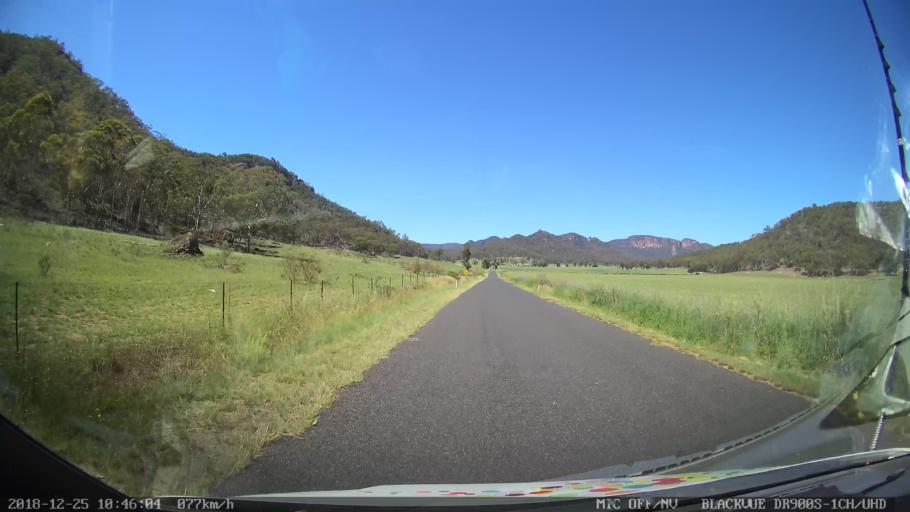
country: AU
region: New South Wales
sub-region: Upper Hunter Shire
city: Merriwa
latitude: -32.4401
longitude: 150.2869
